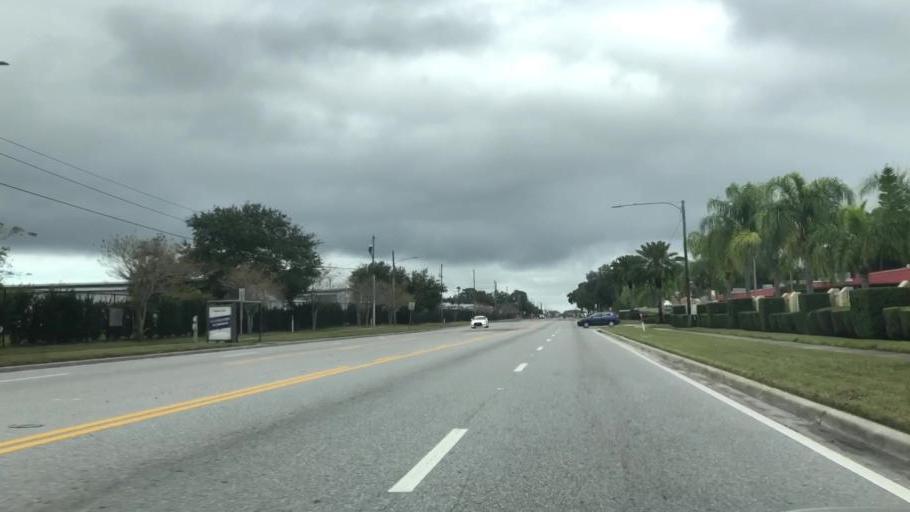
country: US
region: Florida
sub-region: Pinellas County
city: Clearwater
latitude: 27.9719
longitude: -82.7545
